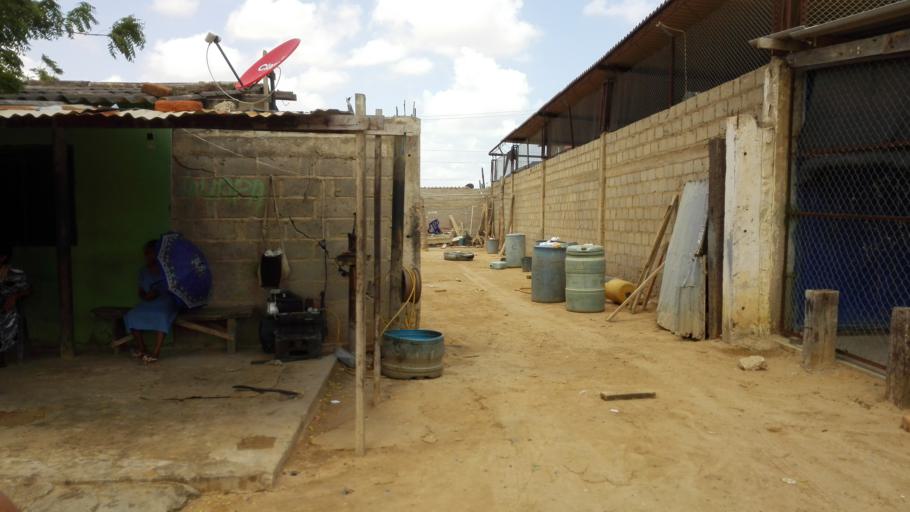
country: CO
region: La Guajira
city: Manaure
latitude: 11.7722
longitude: -72.4458
